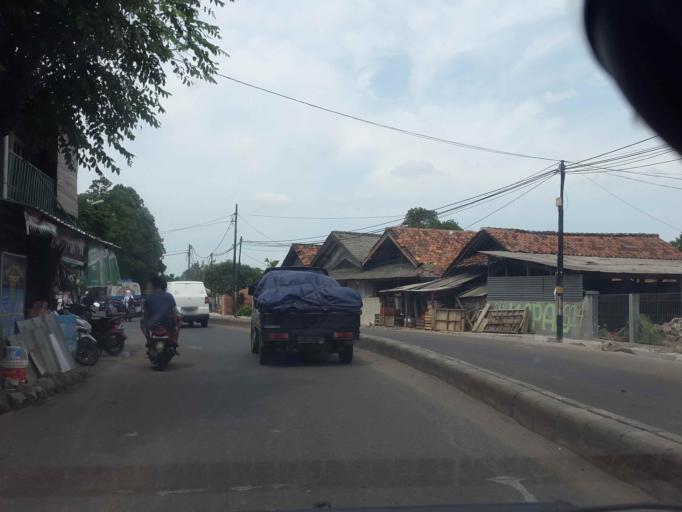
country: ID
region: Banten
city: Tangerang
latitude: -6.1659
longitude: 106.6443
